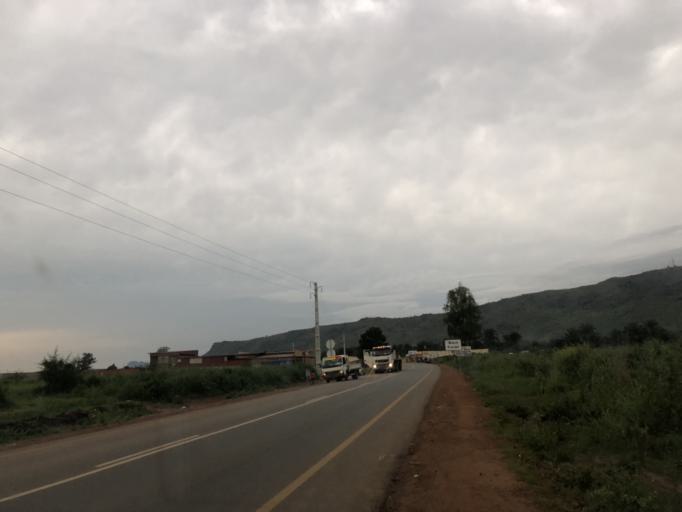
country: AO
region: Cuanza Sul
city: Uacu Cungo
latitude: -11.3460
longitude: 15.1042
